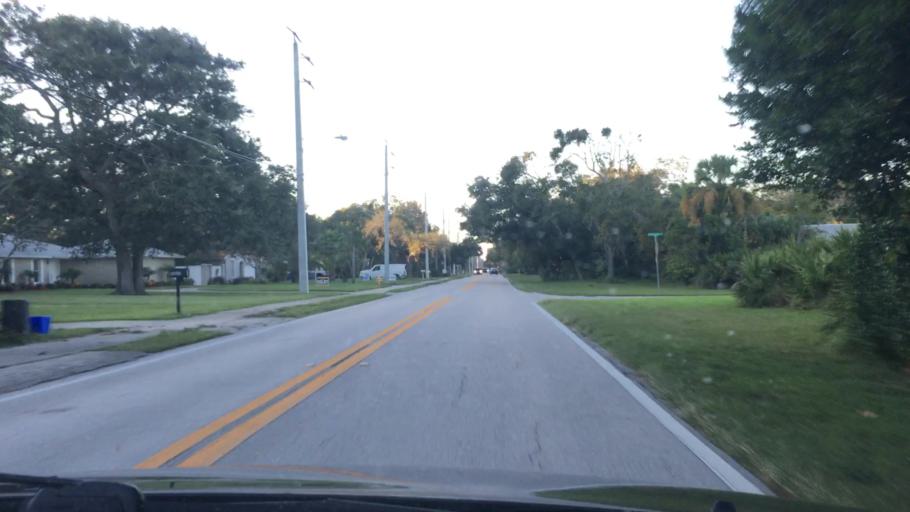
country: US
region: Florida
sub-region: Volusia County
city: Ormond Beach
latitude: 29.3107
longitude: -81.0680
